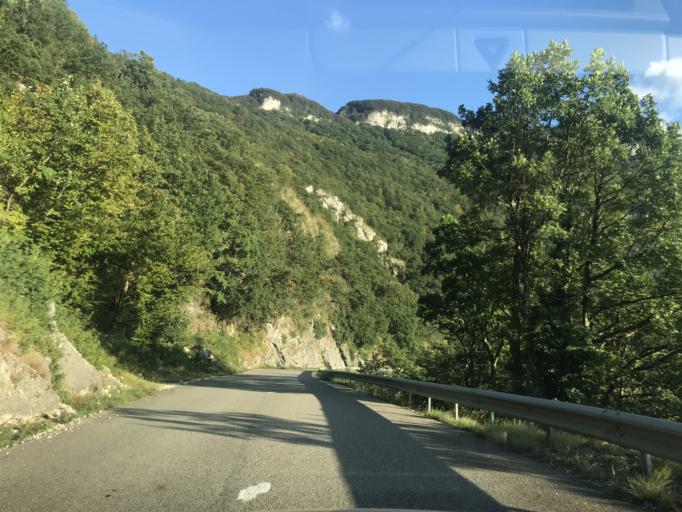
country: FR
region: Rhone-Alpes
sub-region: Departement de la Savoie
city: Le Bourget-du-Lac
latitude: 45.6947
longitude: 5.8344
